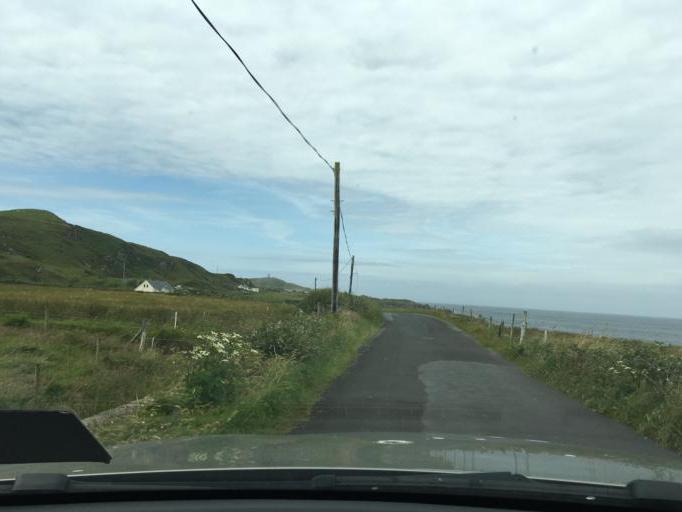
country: IE
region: Ulster
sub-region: County Donegal
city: Carndonagh
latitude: 55.3735
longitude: -7.3439
